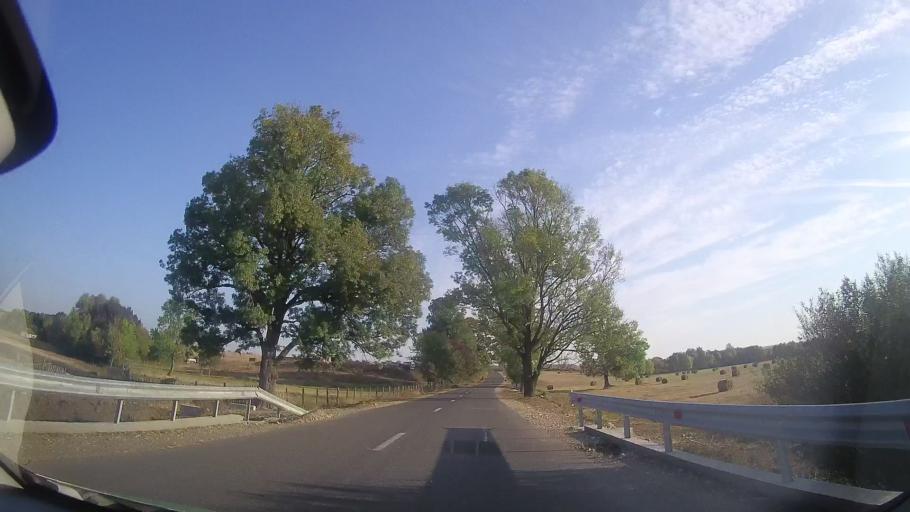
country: RO
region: Timis
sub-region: Comuna Masloc
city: Masloc
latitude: 45.9742
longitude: 21.4959
